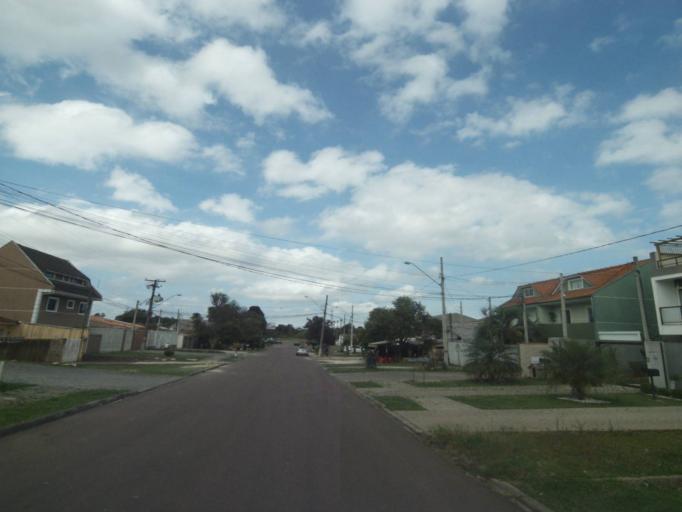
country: BR
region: Parana
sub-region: Pinhais
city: Pinhais
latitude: -25.4117
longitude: -49.2000
